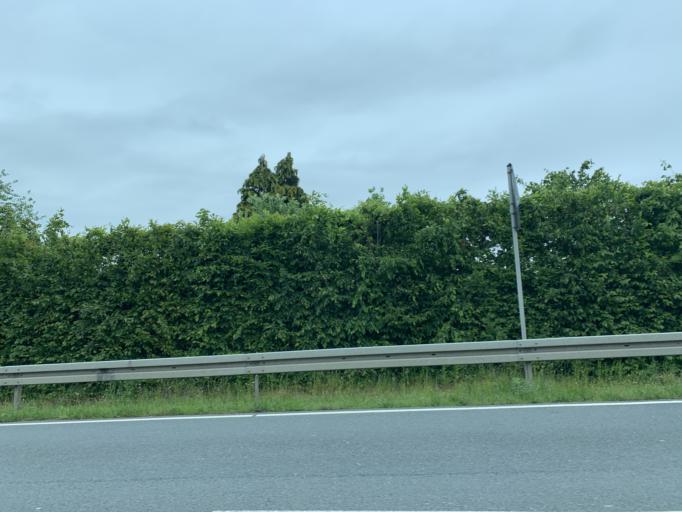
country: DE
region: North Rhine-Westphalia
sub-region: Regierungsbezirk Arnsberg
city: Hamm
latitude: 51.6609
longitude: 7.8366
